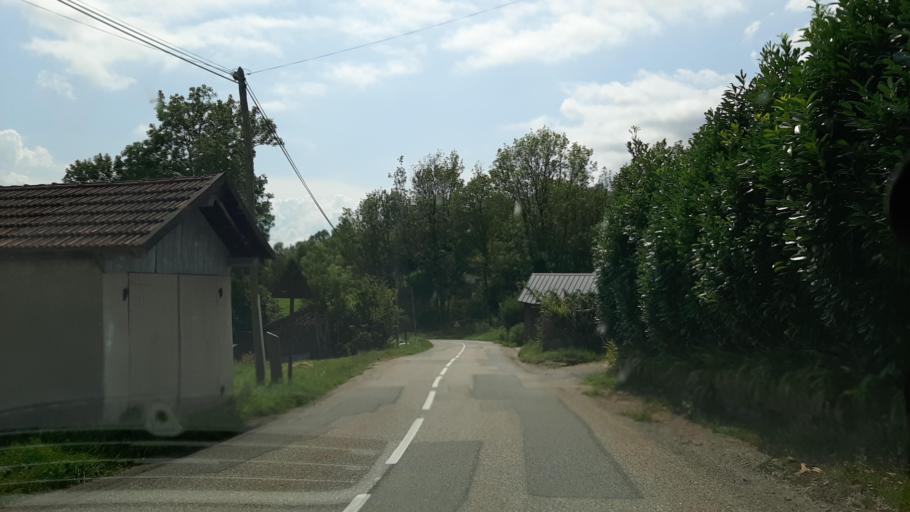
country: FR
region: Rhone-Alpes
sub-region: Departement de la Savoie
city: Frontenex
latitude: 45.6587
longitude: 6.3062
